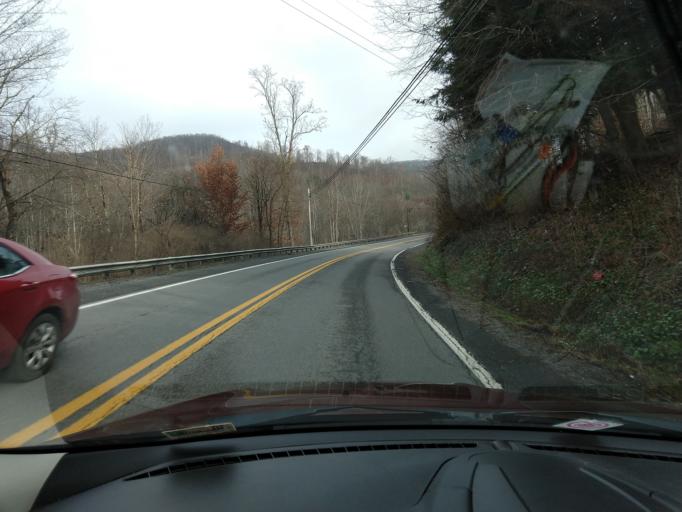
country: US
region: West Virginia
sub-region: Greenbrier County
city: Rainelle
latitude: 38.0505
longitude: -80.7212
